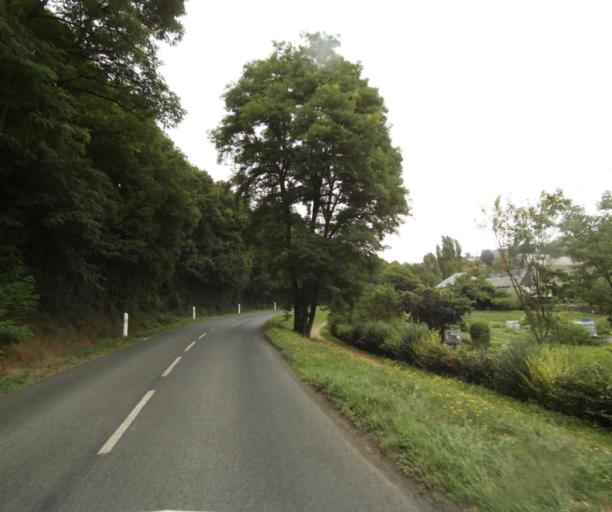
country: FR
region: Pays de la Loire
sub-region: Departement de la Sarthe
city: Juigne-sur-Sarthe
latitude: 47.8586
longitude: -0.2908
